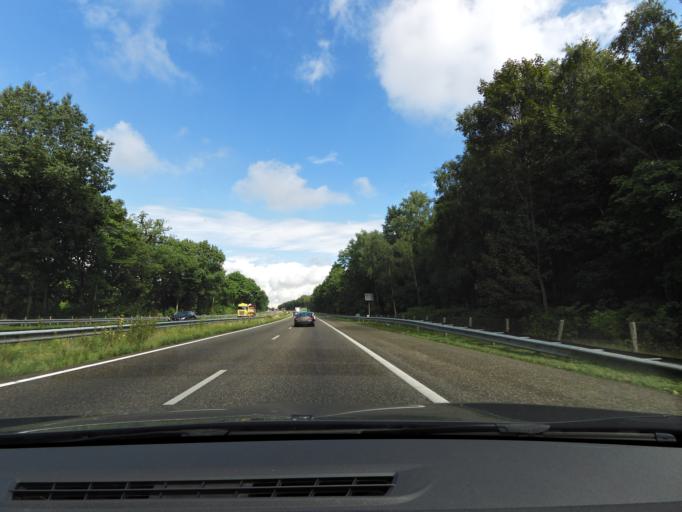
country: NL
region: North Brabant
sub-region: Gemeente Woensdrecht
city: Woensdrecht
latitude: 51.4553
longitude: 4.3134
